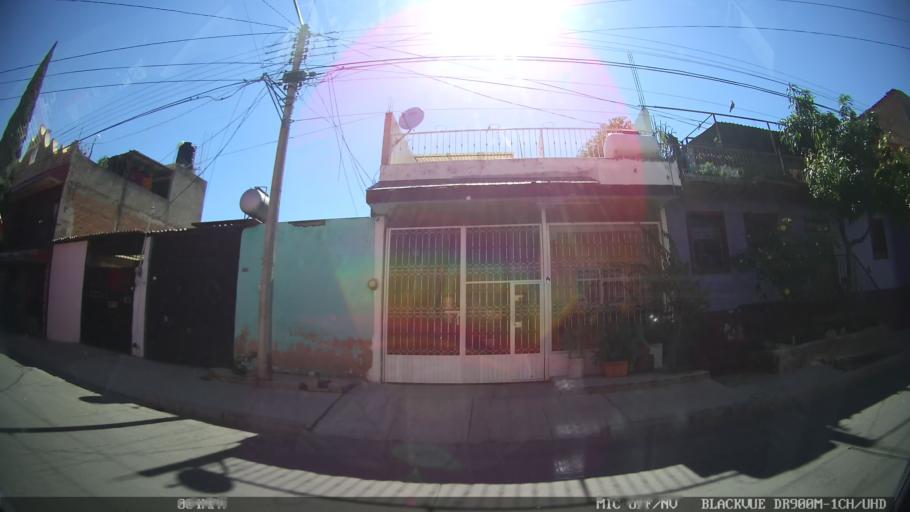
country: MX
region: Jalisco
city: Tlaquepaque
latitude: 20.6569
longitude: -103.2830
